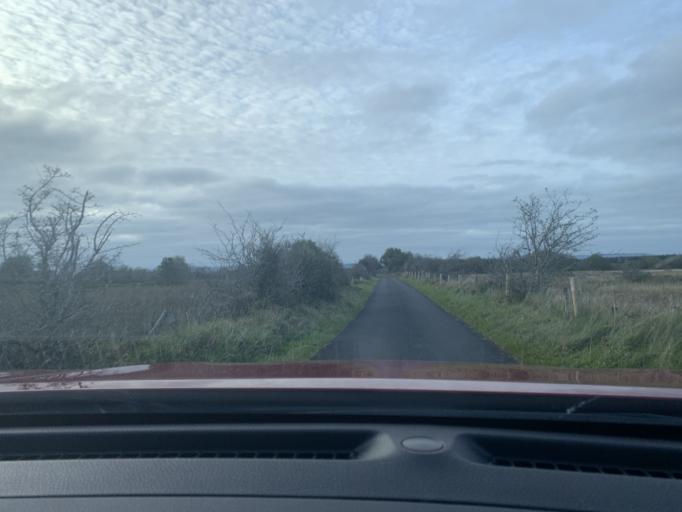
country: IE
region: Connaught
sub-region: Roscommon
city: Ballaghaderreen
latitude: 53.9600
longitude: -8.6022
